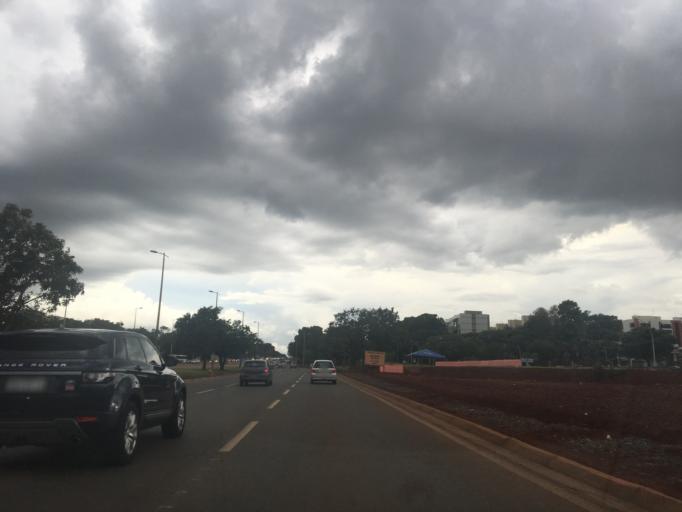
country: BR
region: Federal District
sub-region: Brasilia
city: Brasilia
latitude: -15.7346
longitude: -47.8933
